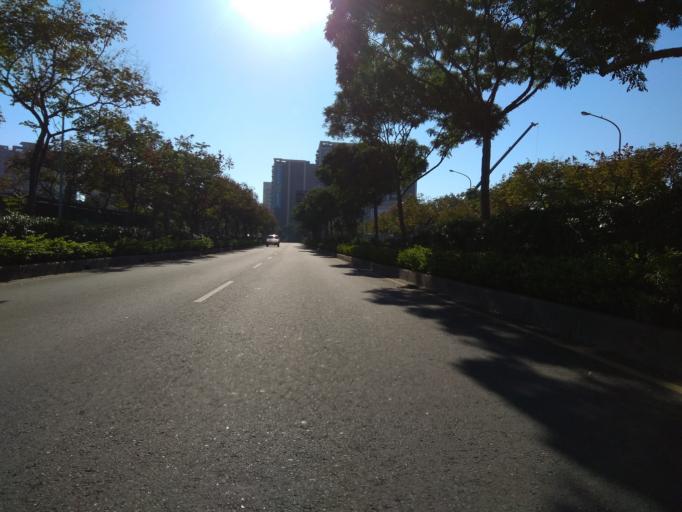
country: TW
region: Taiwan
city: Taoyuan City
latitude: 25.0174
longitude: 121.2234
